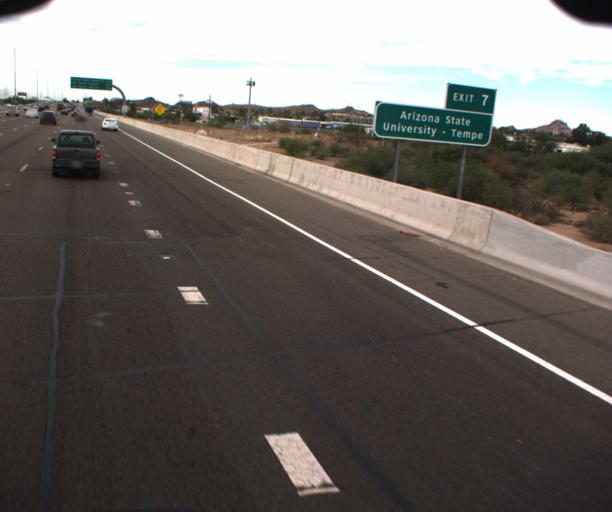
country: US
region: Arizona
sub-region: Maricopa County
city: Tempe
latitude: 33.4362
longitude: -111.9158
